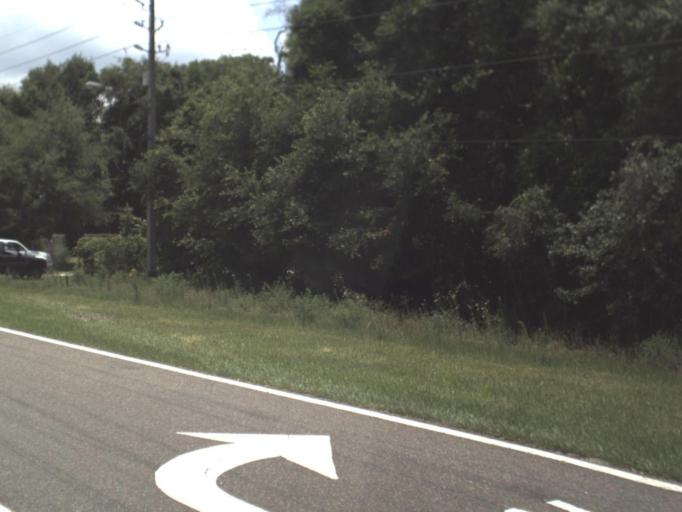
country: US
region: Florida
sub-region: Duval County
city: Jacksonville
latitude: 30.4060
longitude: -81.5656
